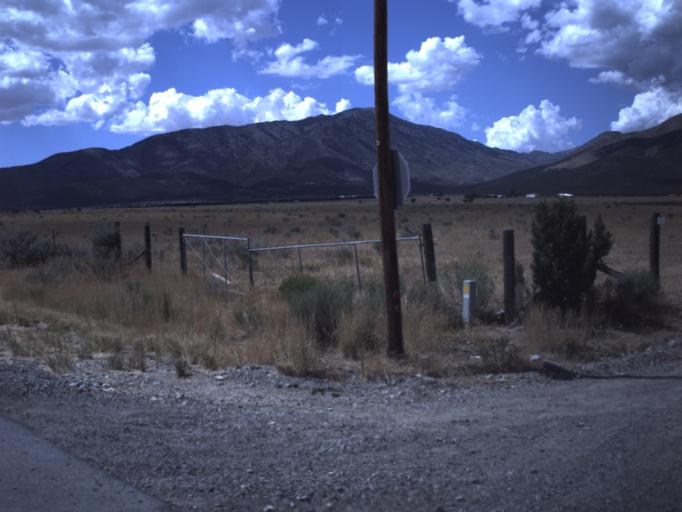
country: US
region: Utah
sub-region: Tooele County
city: Grantsville
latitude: 40.3361
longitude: -112.4988
